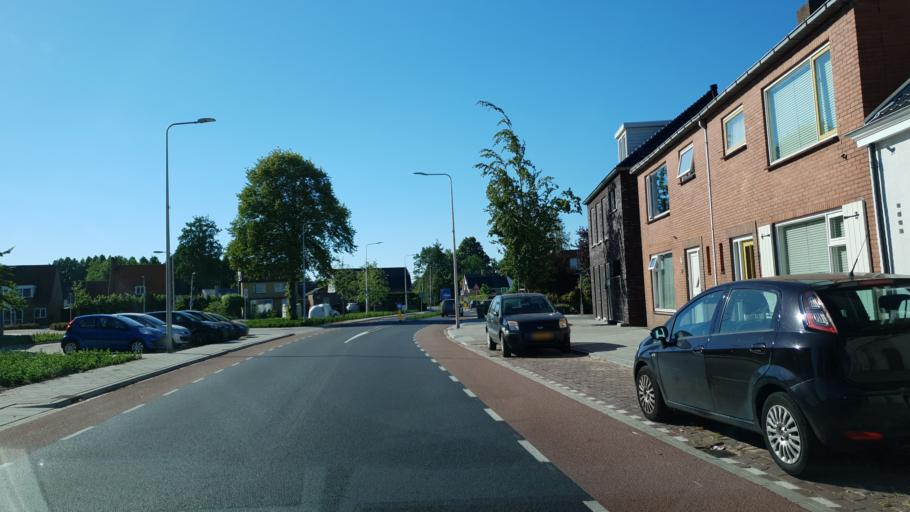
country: NL
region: North Brabant
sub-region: Gemeente Zundert
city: Zundert
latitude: 51.4704
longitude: 4.6570
